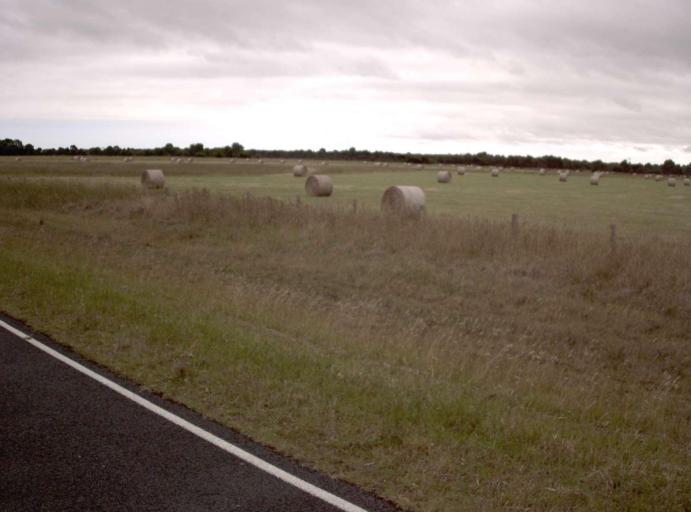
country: AU
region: Victoria
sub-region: Wellington
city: Sale
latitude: -38.5650
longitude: 146.8795
